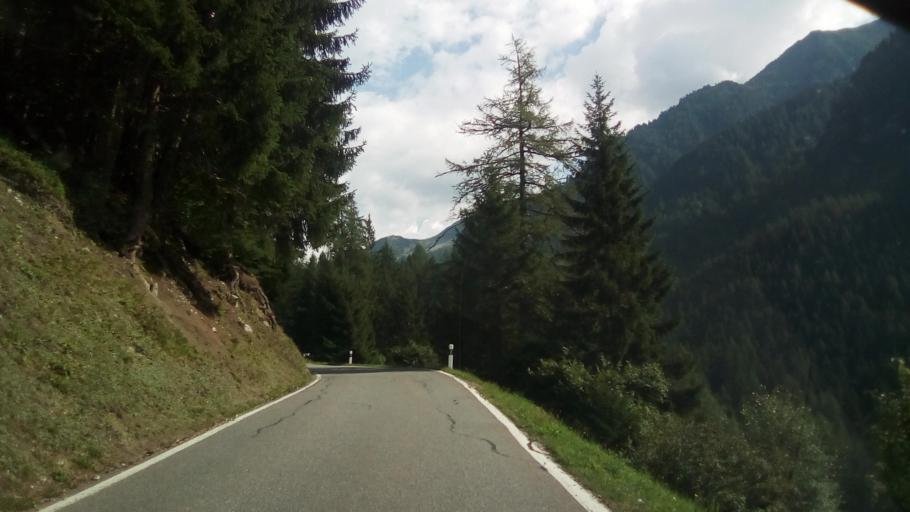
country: CH
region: Valais
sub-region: Martigny District
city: Martigny-Combe
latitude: 46.0540
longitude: 7.0837
